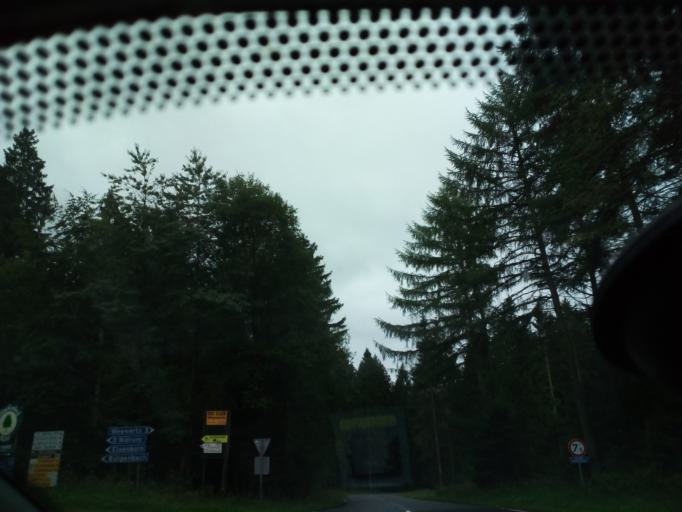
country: BE
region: Wallonia
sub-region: Province de Liege
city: Butgenbach
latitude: 50.4626
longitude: 6.1710
